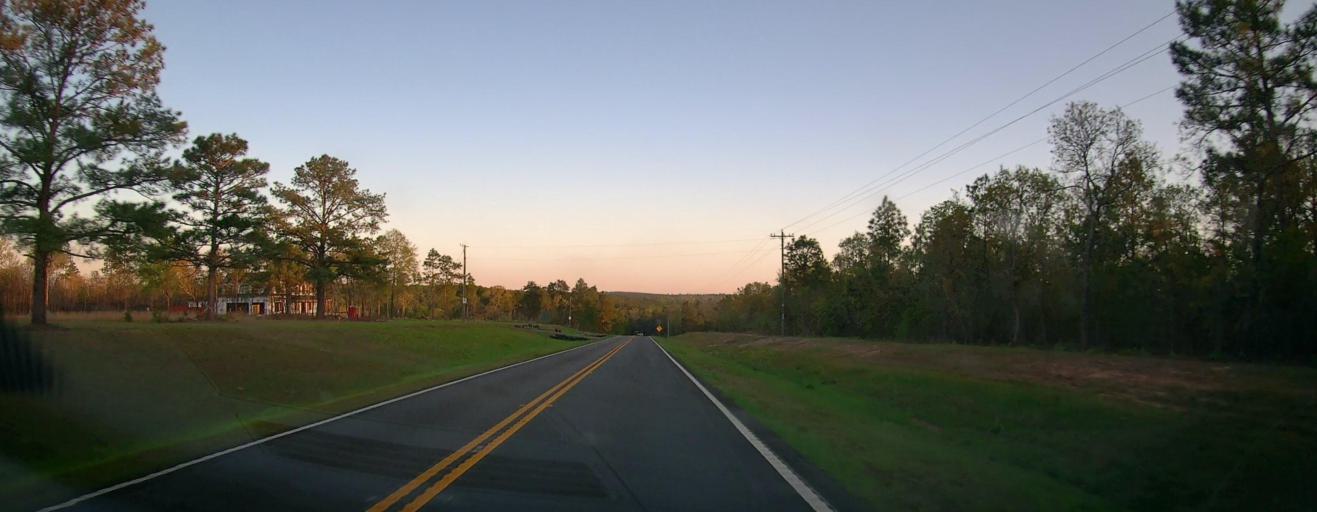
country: US
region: Georgia
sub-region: Marion County
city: Buena Vista
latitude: 32.4511
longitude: -84.6252
